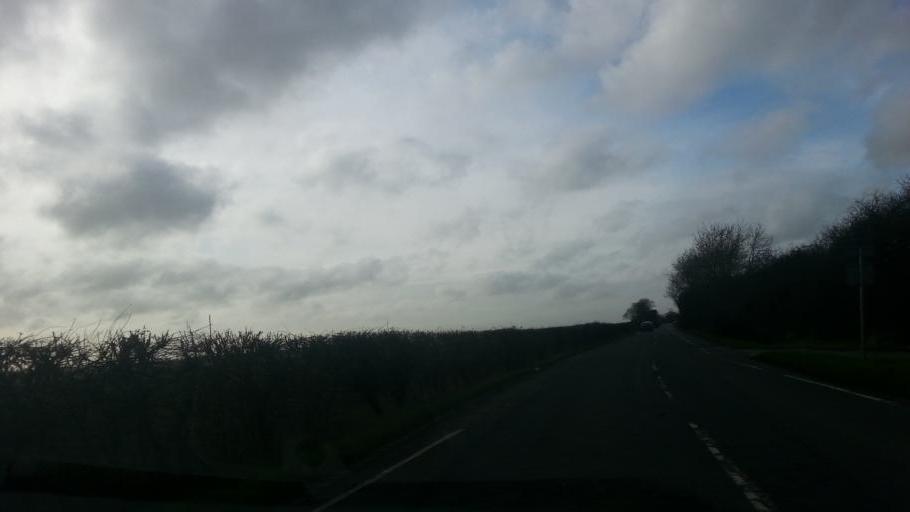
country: GB
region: England
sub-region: District of Rutland
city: Wing
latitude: 52.6345
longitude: -0.6765
